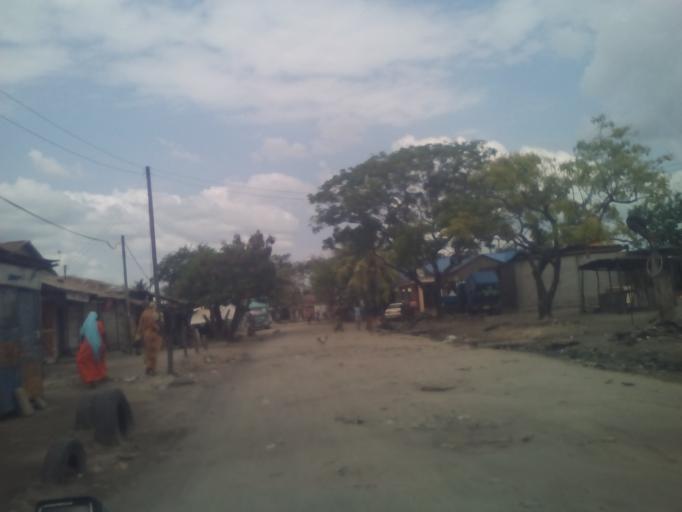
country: TZ
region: Dar es Salaam
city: Dar es Salaam
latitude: -6.8633
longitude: 39.2237
